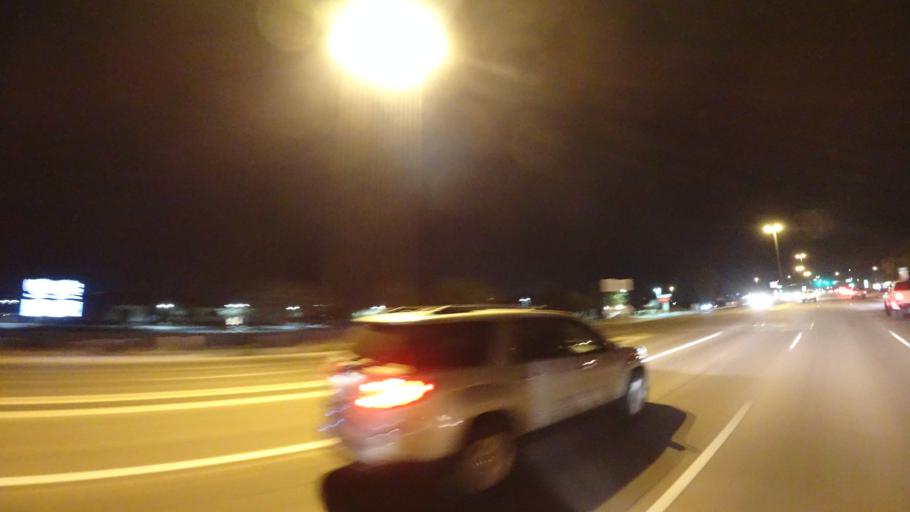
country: US
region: Arizona
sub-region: Maricopa County
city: Gilbert
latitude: 33.3236
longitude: -111.7557
